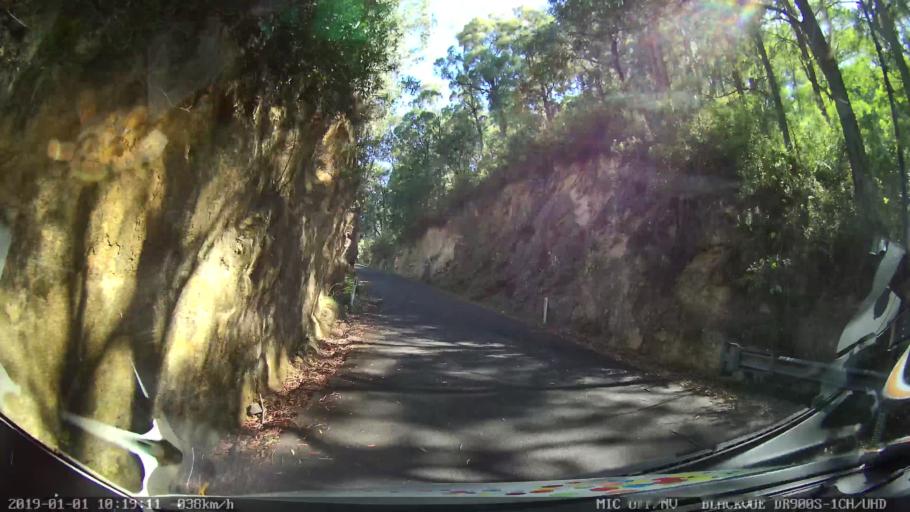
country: AU
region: New South Wales
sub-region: Snowy River
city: Jindabyne
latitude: -36.0862
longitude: 148.1859
